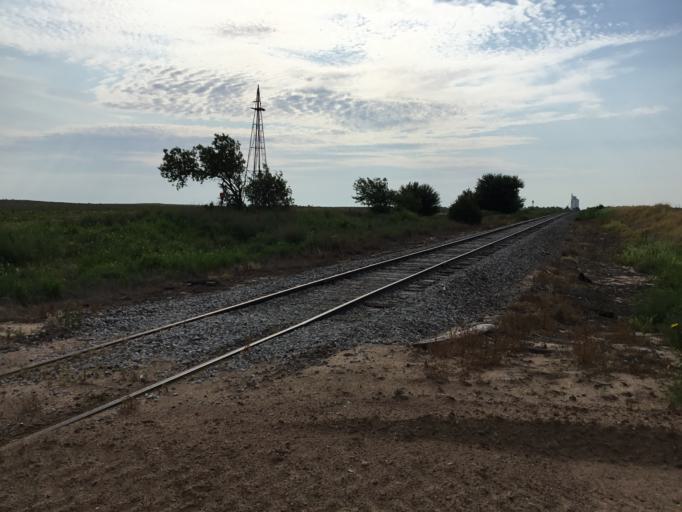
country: US
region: Kansas
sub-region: Barber County
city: Medicine Lodge
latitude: 37.4726
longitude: -98.5742
